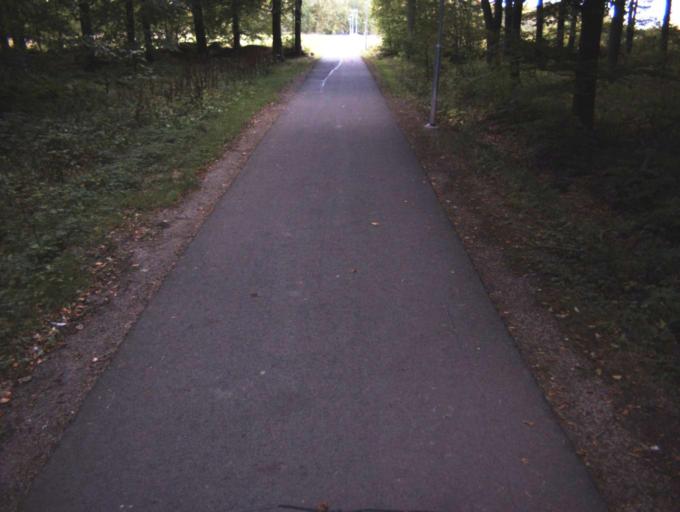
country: SE
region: Skane
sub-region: Helsingborg
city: Helsingborg
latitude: 56.0837
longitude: 12.6797
